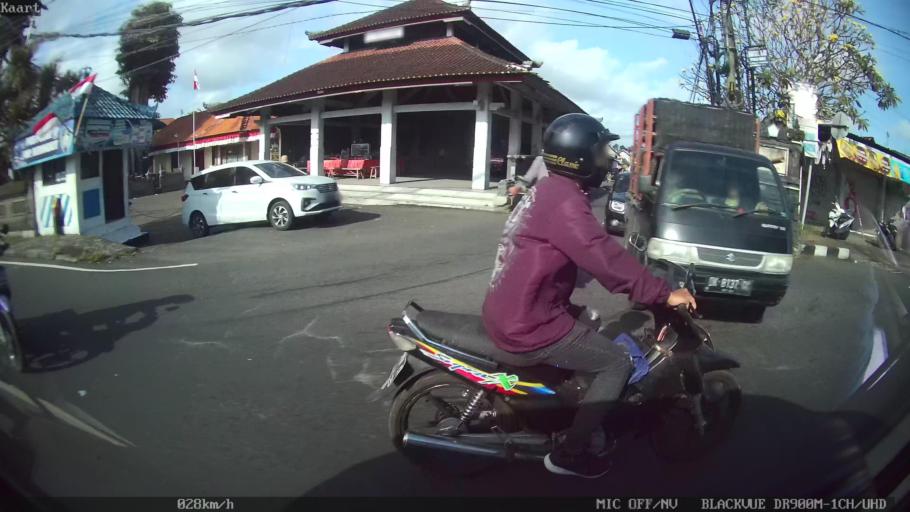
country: ID
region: Bali
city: Banjar Jumbayah
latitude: -8.5644
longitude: 115.1736
